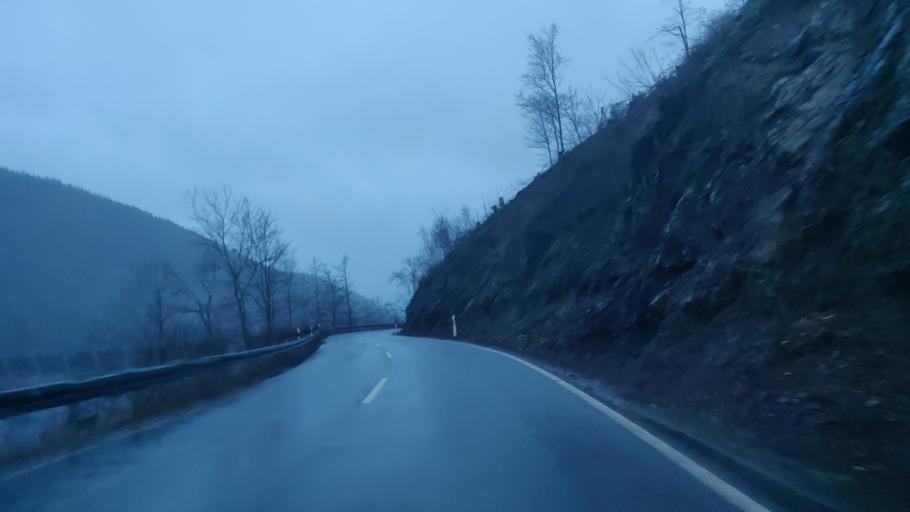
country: DE
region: Lower Saxony
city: Sankt Andreasberg
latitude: 51.6680
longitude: 10.5399
